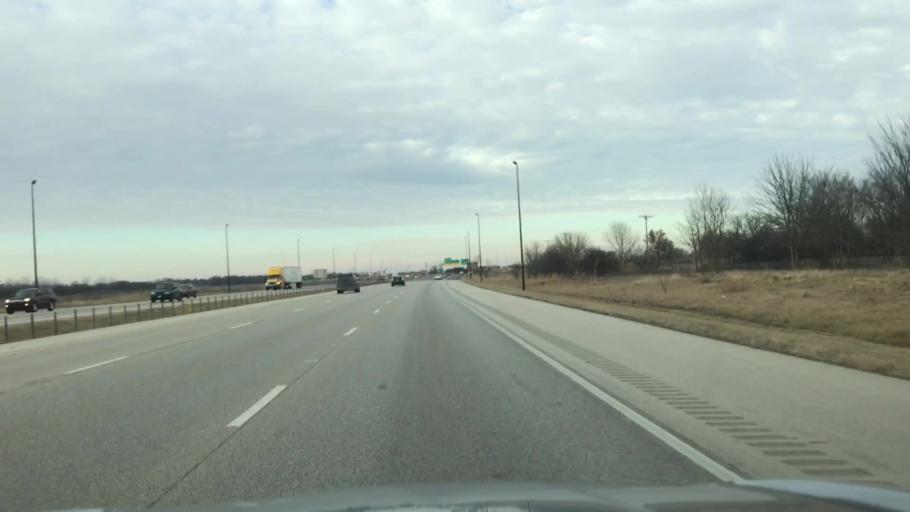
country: US
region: Illinois
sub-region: Sangamon County
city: Southern View
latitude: 39.7296
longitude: -89.6440
